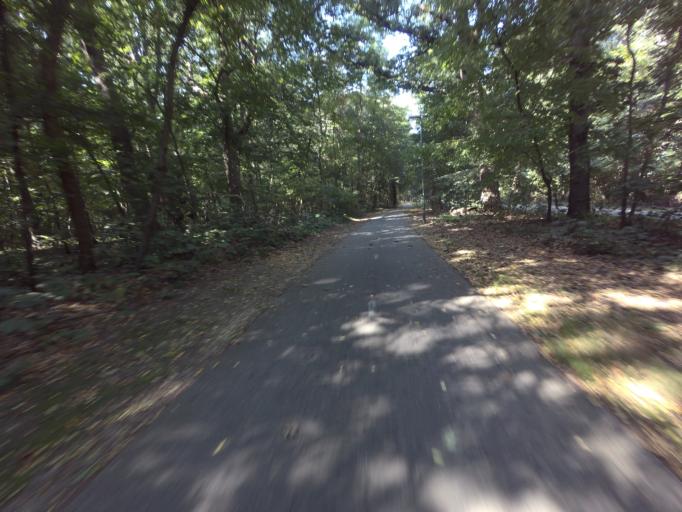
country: NL
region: Limburg
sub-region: Gemeente Roerdalen
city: Sint Odilienberg
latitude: 51.1442
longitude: 6.0113
